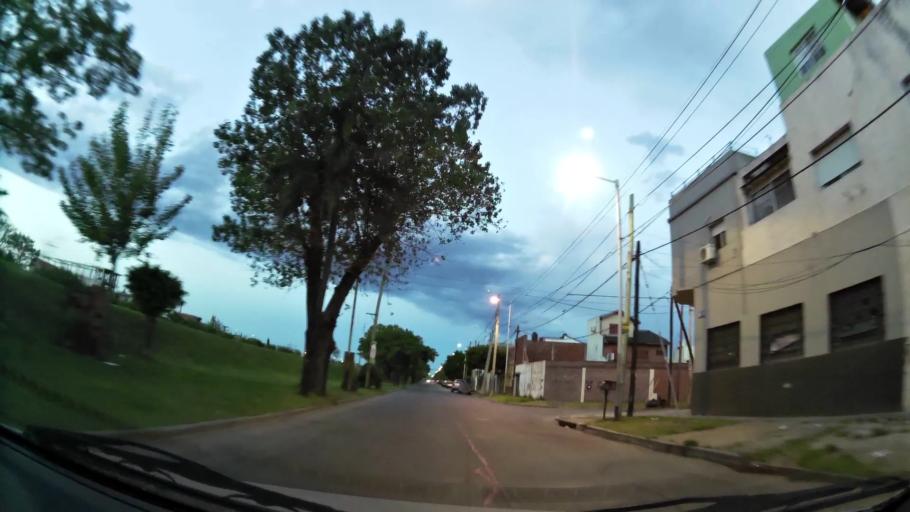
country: AR
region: Buenos Aires
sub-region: Partido de Avellaneda
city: Avellaneda
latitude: -34.6898
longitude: -58.3254
